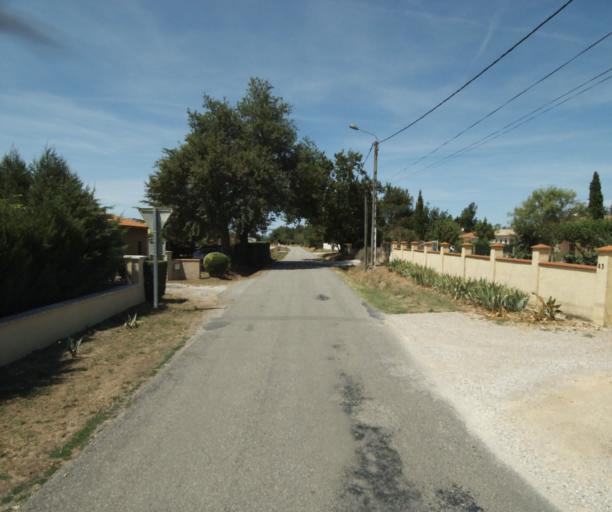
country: FR
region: Midi-Pyrenees
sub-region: Departement de la Haute-Garonne
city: Revel
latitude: 43.4862
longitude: 2.0273
